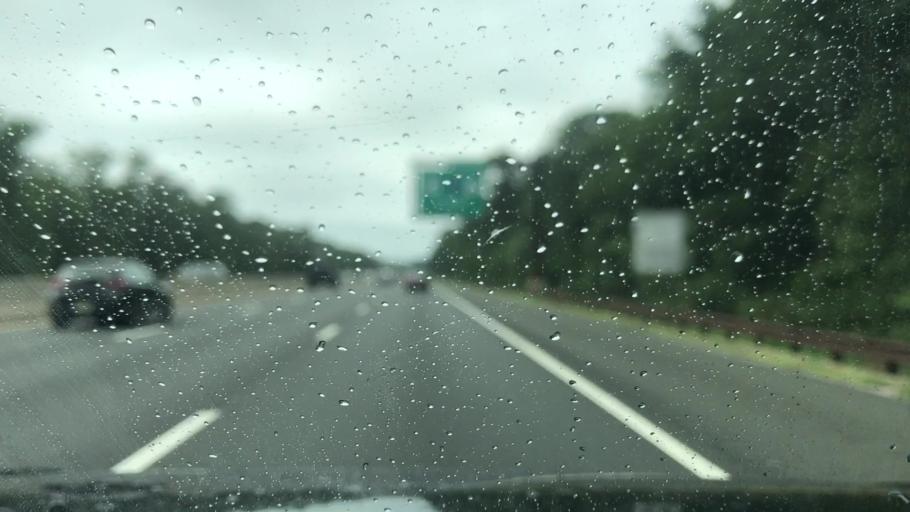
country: US
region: New Jersey
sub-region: Ocean County
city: Silver Ridge
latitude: 39.9712
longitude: -74.2091
